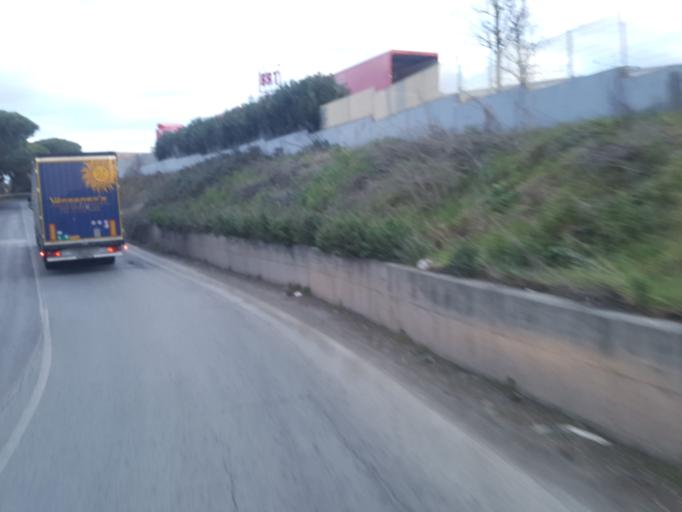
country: IT
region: Latium
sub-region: Citta metropolitana di Roma Capitale
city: Area Produttiva
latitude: 41.6985
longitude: 12.5367
